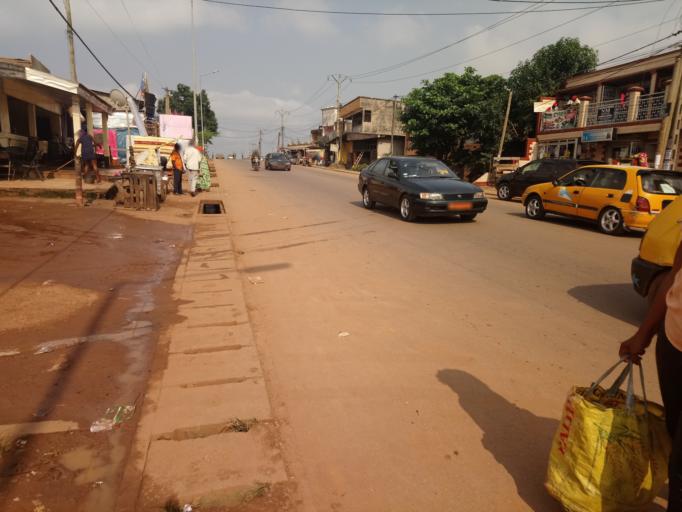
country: CM
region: Centre
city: Yaounde
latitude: 3.8254
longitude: 11.5057
